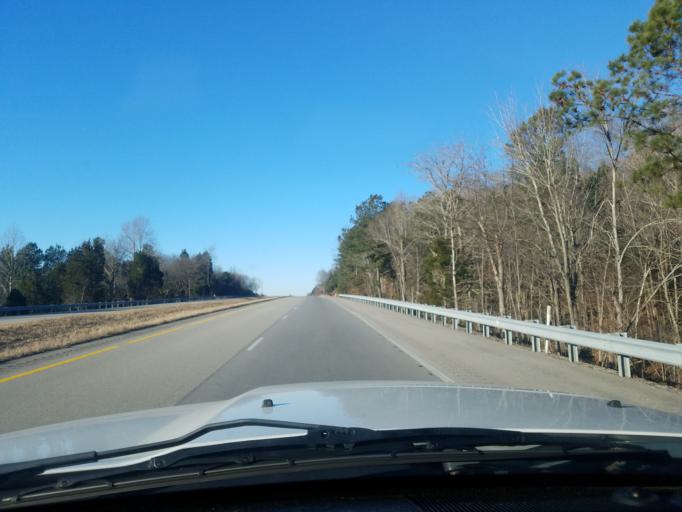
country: US
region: Kentucky
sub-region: Ohio County
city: Oak Grove
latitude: 37.3916
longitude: -86.6170
